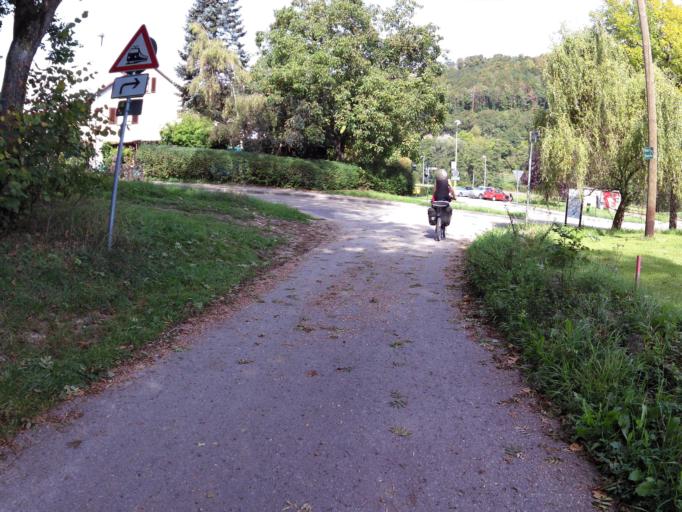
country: DE
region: Baden-Wuerttemberg
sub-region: Karlsruhe Region
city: Horb am Neckar
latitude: 48.4491
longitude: 8.7282
